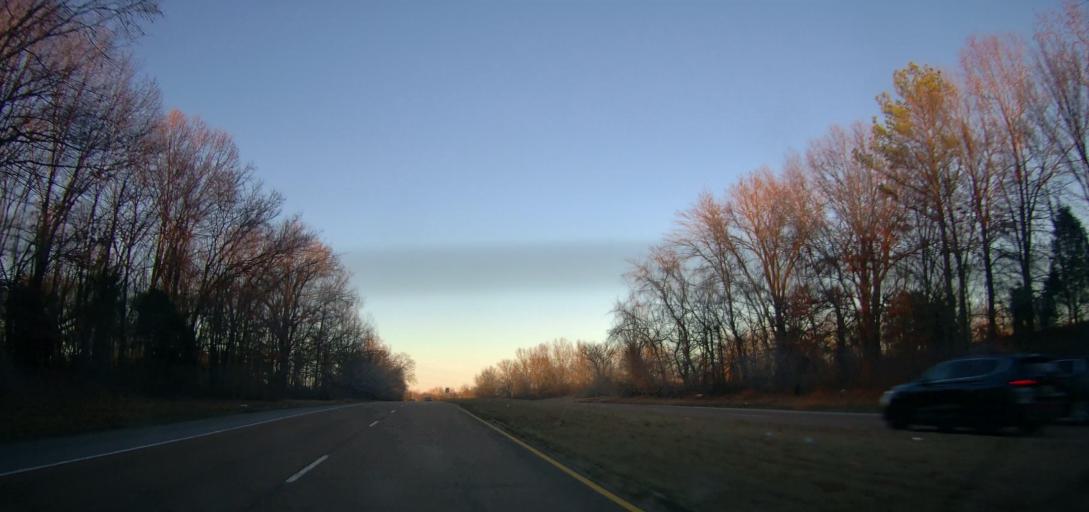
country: US
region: Tennessee
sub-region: Shelby County
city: Bartlett
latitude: 35.2491
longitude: -89.8958
